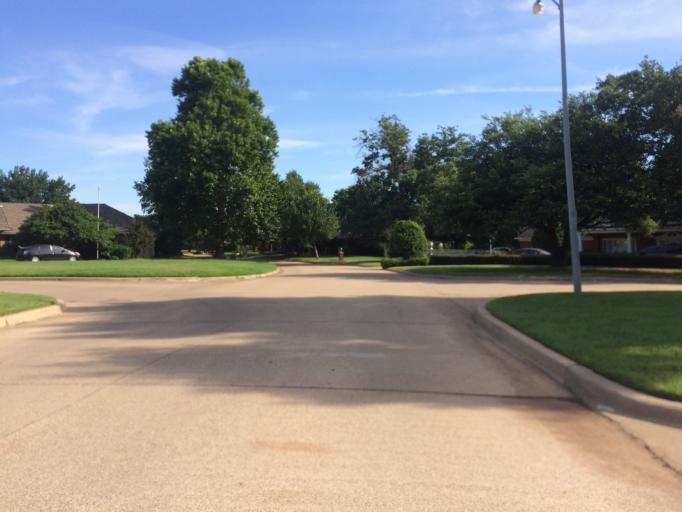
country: US
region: Oklahoma
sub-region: Cleveland County
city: Norman
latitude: 35.2259
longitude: -97.4721
